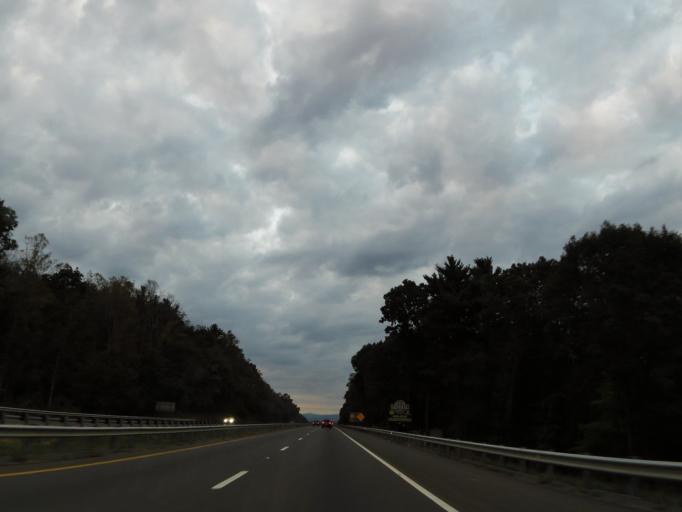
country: US
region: North Carolina
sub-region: Buncombe County
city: Woodfin
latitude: 35.6600
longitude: -82.5835
